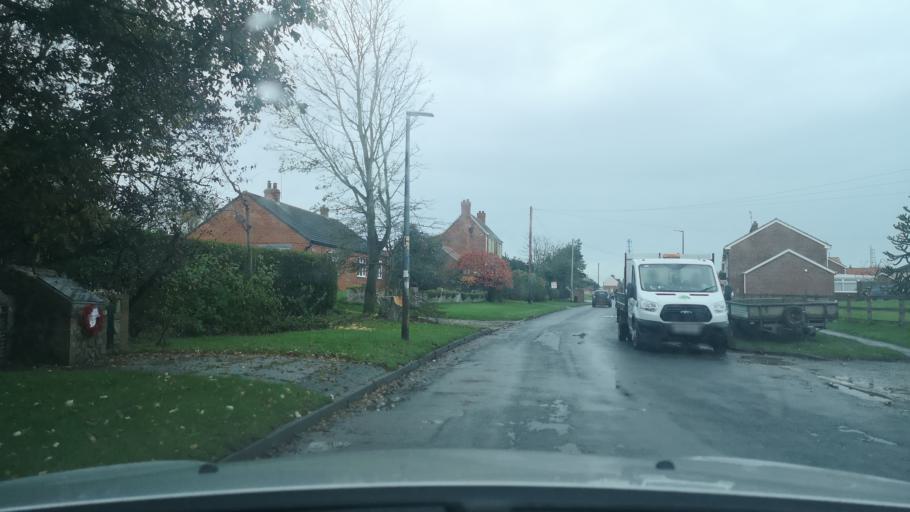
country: GB
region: England
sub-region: East Riding of Yorkshire
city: Easington
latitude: 53.6509
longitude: 0.1140
